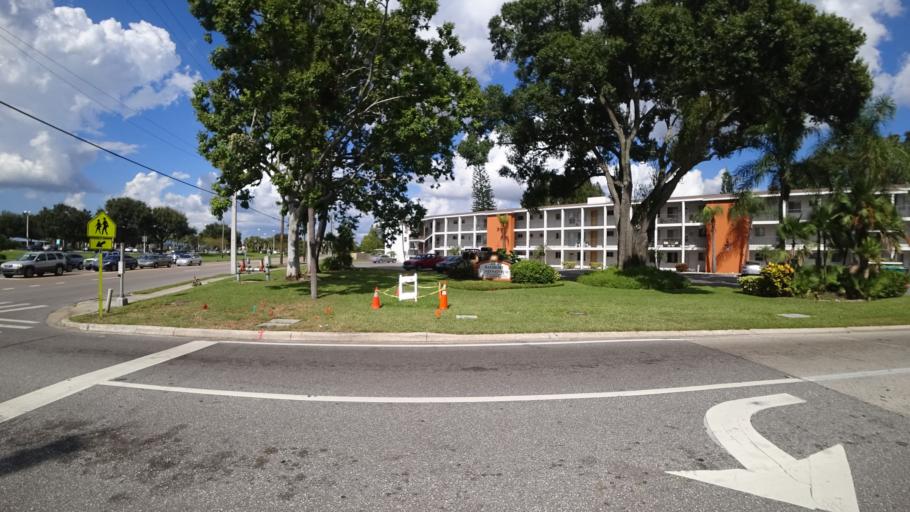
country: US
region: Florida
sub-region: Manatee County
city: Bayshore Gardens
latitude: 27.4359
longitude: -82.5876
